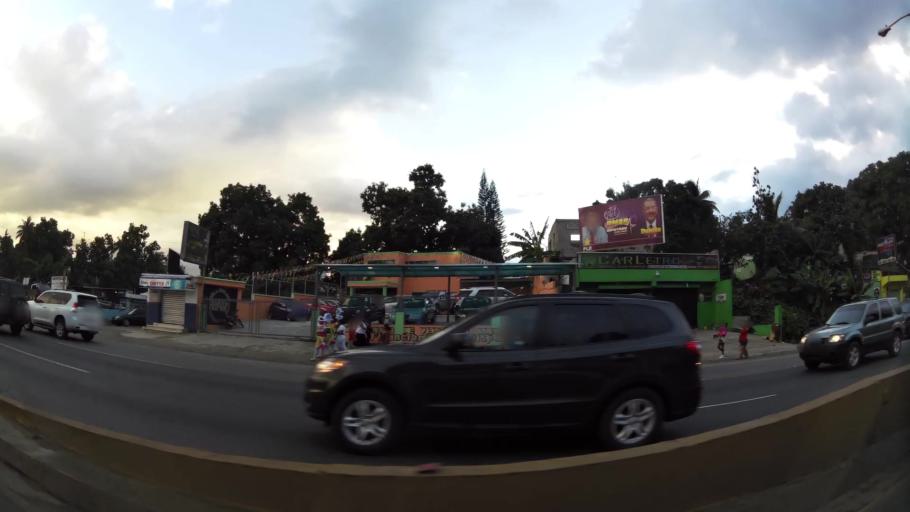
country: DO
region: Santo Domingo
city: Santo Domingo Oeste
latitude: 18.5495
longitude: -70.0488
